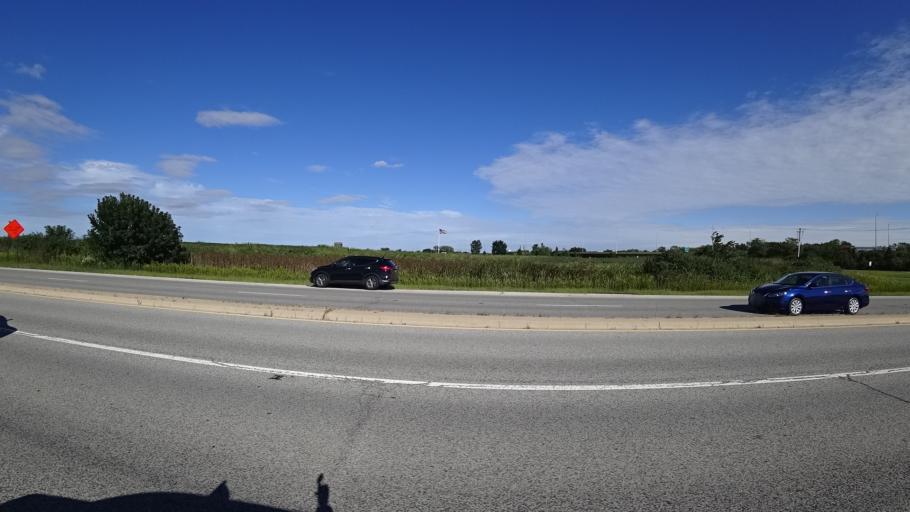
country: US
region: Illinois
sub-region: Cook County
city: Country Club Hills
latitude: 41.5725
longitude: -87.7332
